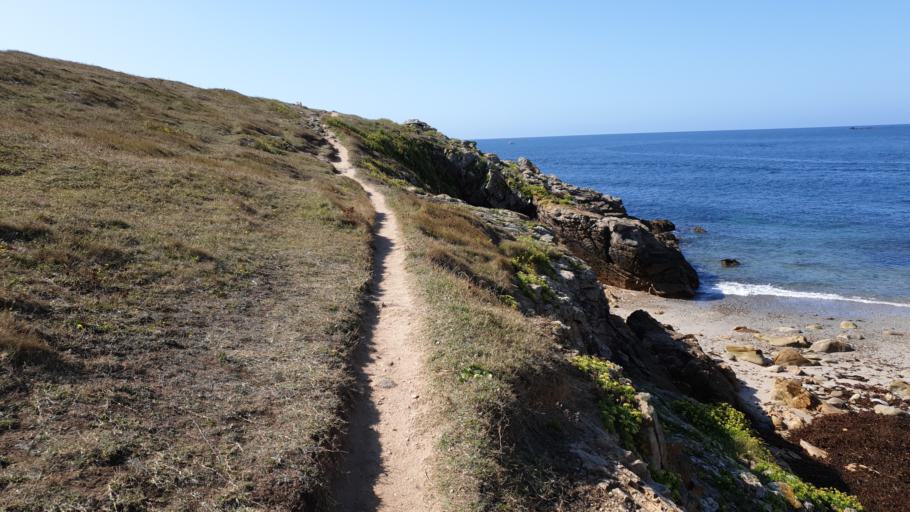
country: FR
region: Brittany
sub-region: Departement du Morbihan
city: Saint-Gildas-de-Rhuys
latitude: 47.3459
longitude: -2.8904
